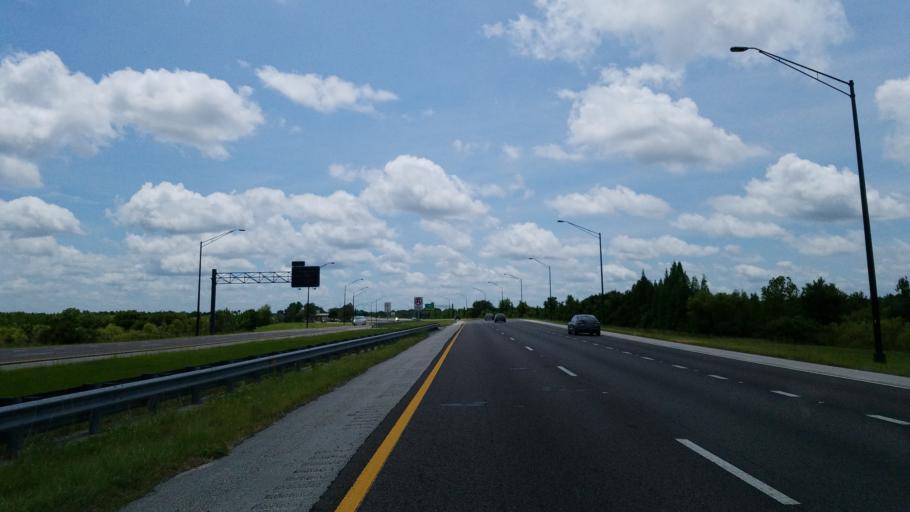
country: US
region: Florida
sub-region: Polk County
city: Winston
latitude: 28.0035
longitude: -82.0073
